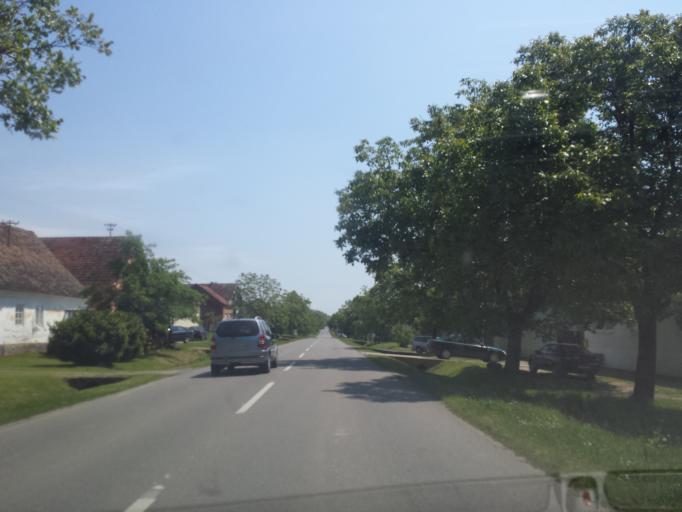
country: HR
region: Brodsko-Posavska
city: Oriovac
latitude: 45.1691
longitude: 17.7388
